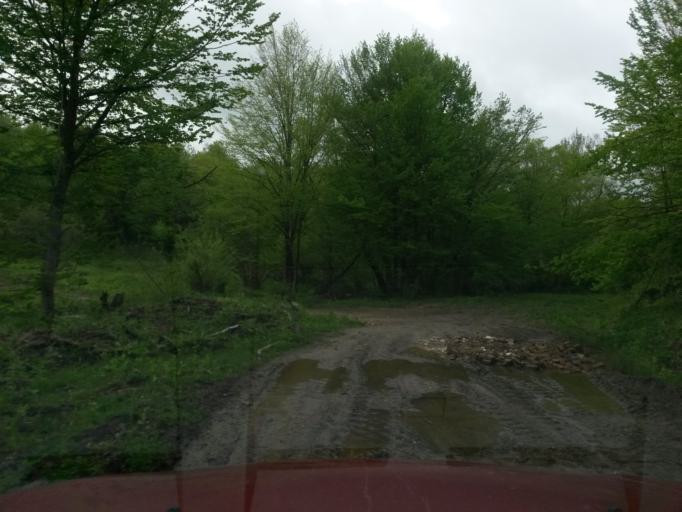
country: SK
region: Kosicky
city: Sobrance
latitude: 48.8303
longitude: 22.3092
